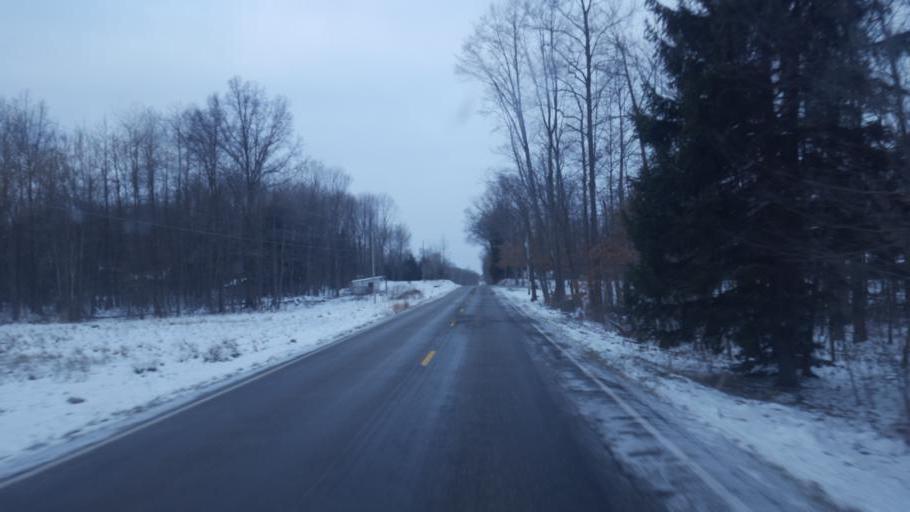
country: US
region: Pennsylvania
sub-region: Mercer County
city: Stoneboro
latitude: 41.4057
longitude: -80.0230
